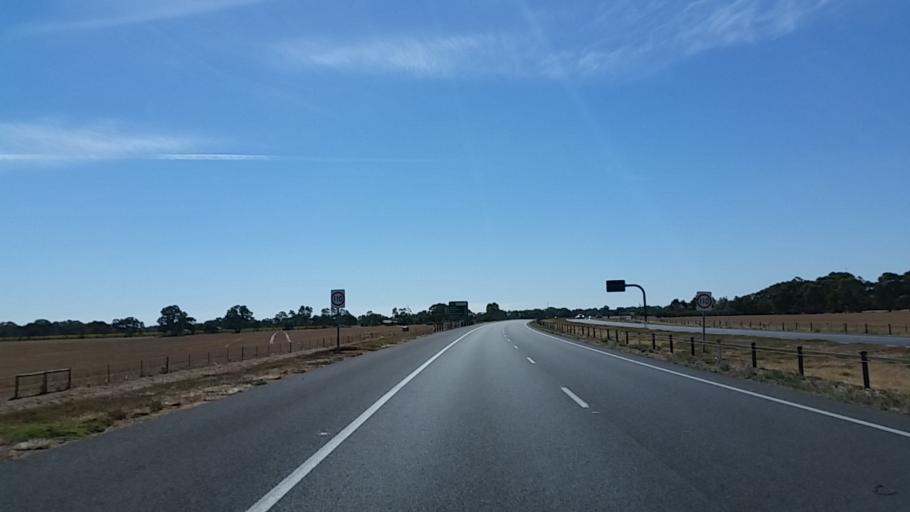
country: AU
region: South Australia
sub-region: Playford
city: Angle Vale
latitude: -34.6273
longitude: 138.6727
